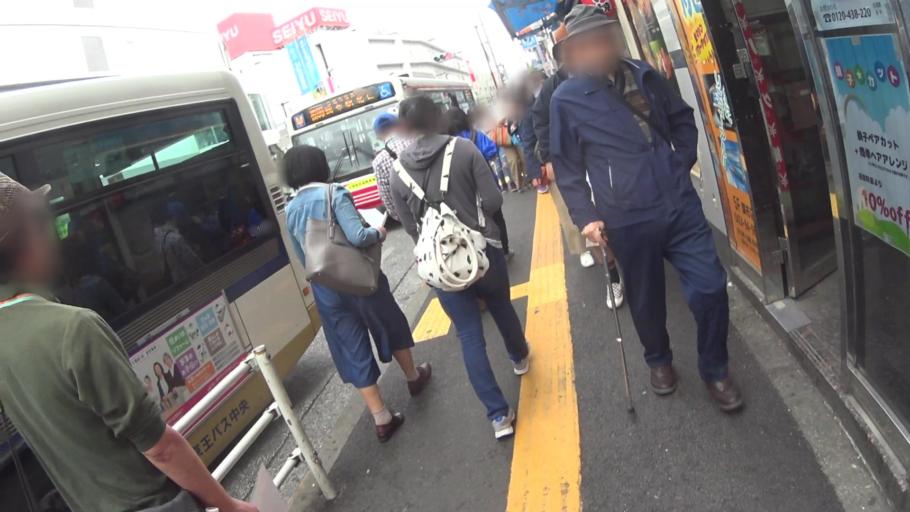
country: JP
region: Tokyo
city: Chofugaoka
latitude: 35.6498
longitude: 139.5447
